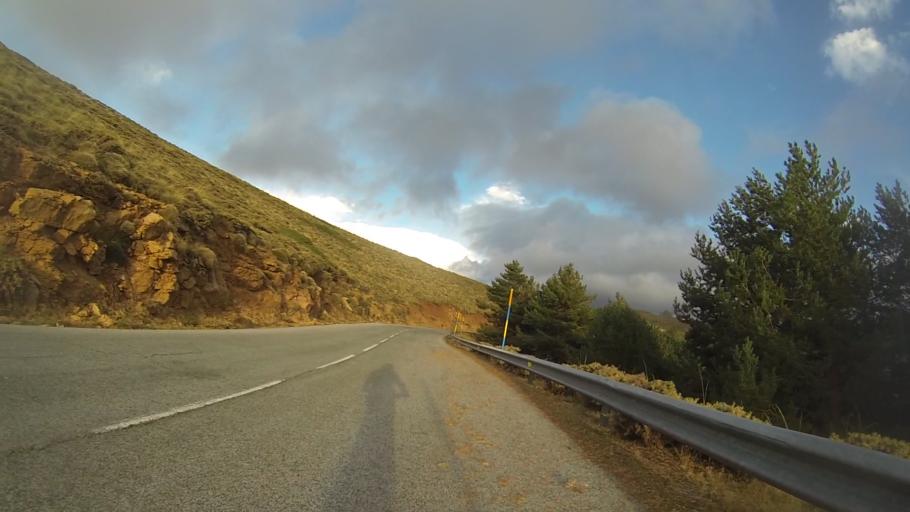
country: ES
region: Andalusia
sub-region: Provincia de Granada
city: Guejar-Sierra
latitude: 37.1167
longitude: -3.4270
